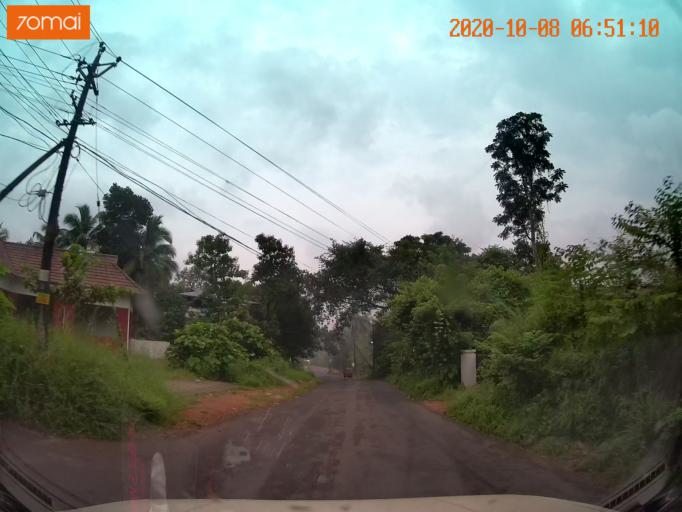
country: IN
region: Kerala
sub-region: Thrissur District
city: Kunnamkulam
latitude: 10.6889
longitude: 76.0959
